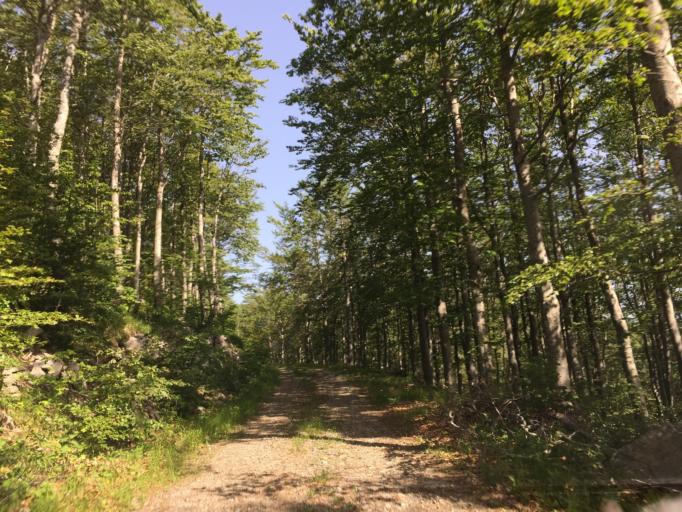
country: HR
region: Primorsko-Goranska
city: Podhum
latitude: 45.4250
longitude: 14.5841
